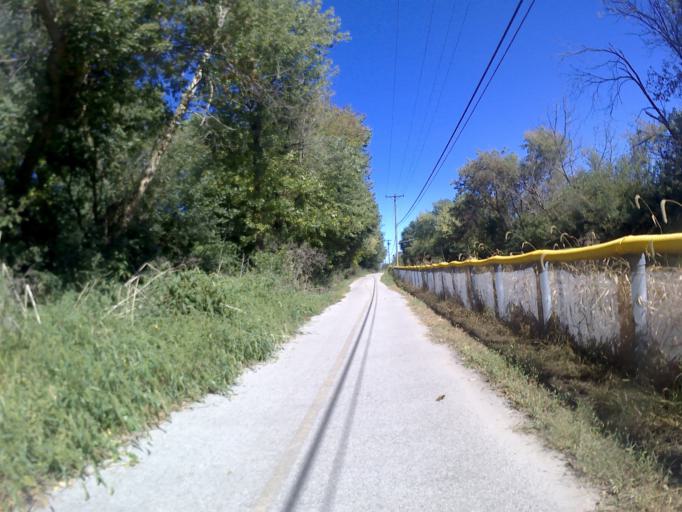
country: US
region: Illinois
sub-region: Cook County
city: Lemont
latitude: 41.6758
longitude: -88.0188
